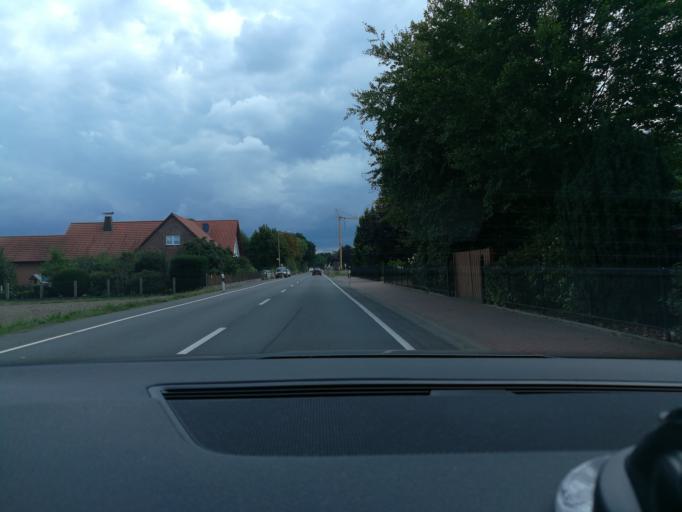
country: DE
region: North Rhine-Westphalia
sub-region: Regierungsbezirk Detmold
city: Minden
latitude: 52.3203
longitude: 8.8744
